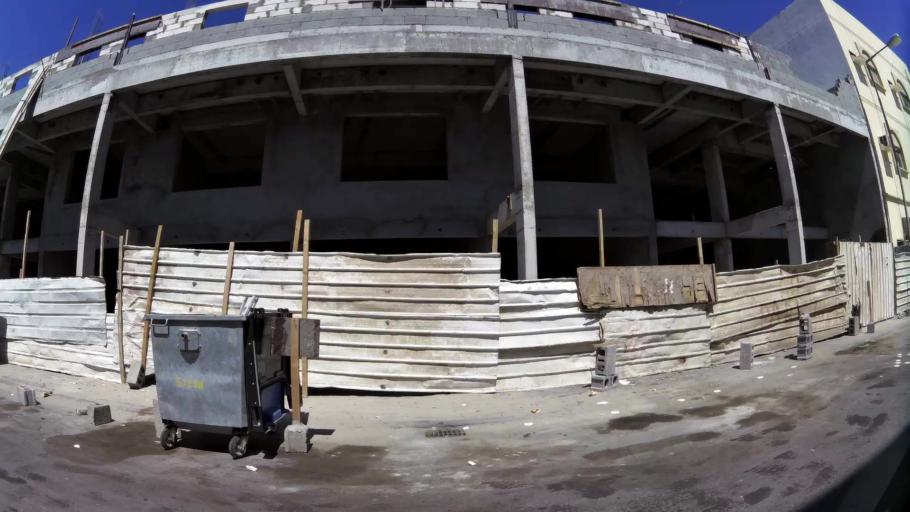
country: BH
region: Muharraq
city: Al Muharraq
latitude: 26.2717
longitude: 50.6080
